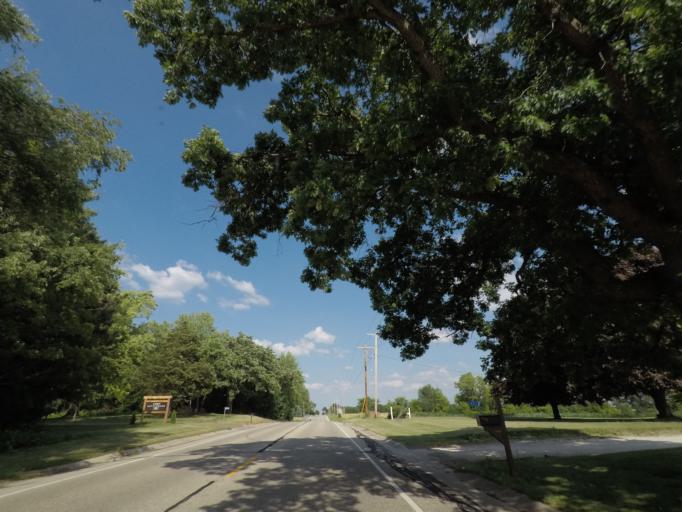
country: US
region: Wisconsin
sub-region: Walworth County
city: East Troy
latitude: 42.7930
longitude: -88.4762
